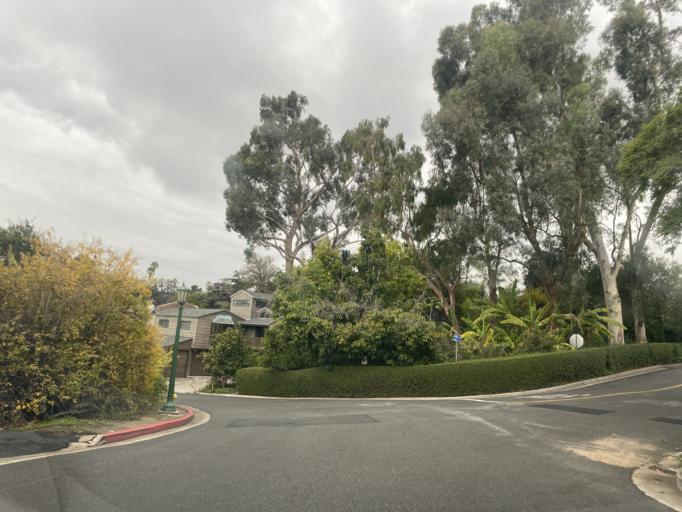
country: US
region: California
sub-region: Orange County
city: Fullerton
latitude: 33.8815
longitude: -117.9188
